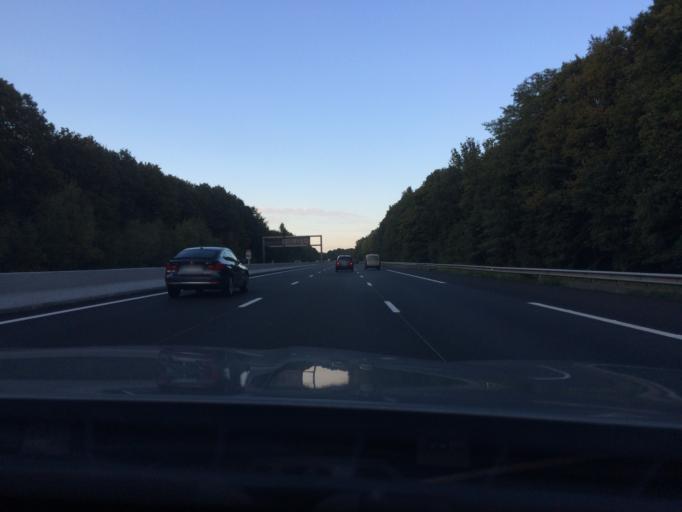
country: FR
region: Ile-de-France
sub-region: Departement de l'Essonne
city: Soisy-sur-Ecole
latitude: 48.4960
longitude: 2.5130
